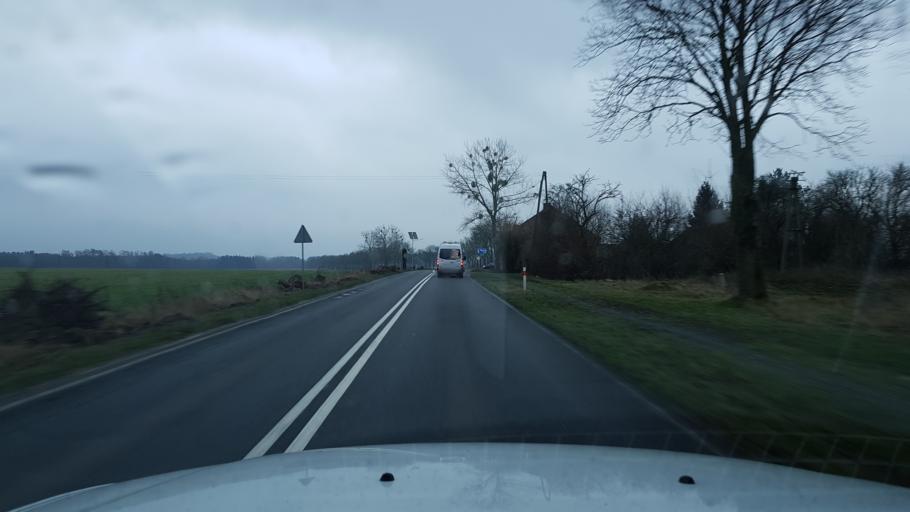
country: PL
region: West Pomeranian Voivodeship
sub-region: Powiat gryficki
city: Gryfice
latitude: 53.8707
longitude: 15.2161
